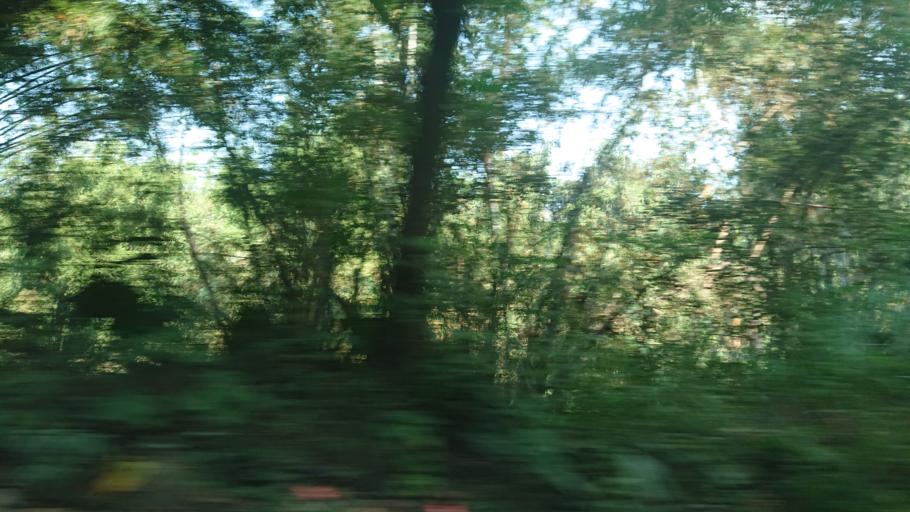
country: TW
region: Taiwan
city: Lugu
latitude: 23.7126
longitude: 120.6690
